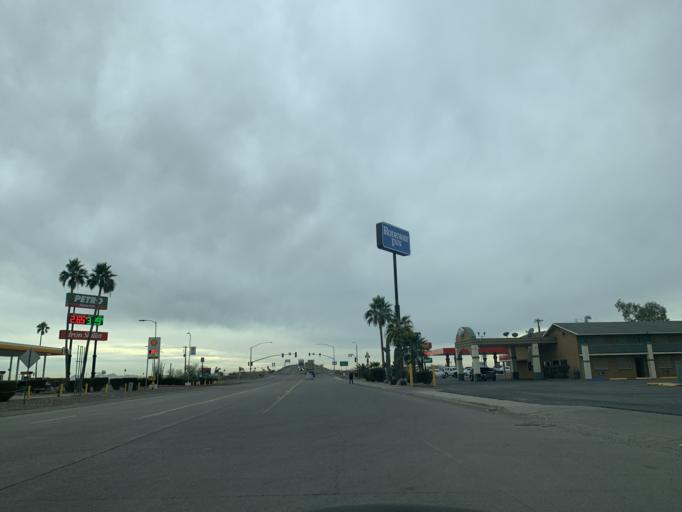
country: US
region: Arizona
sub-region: Pinal County
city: Arizona City
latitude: 32.8131
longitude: -111.6711
